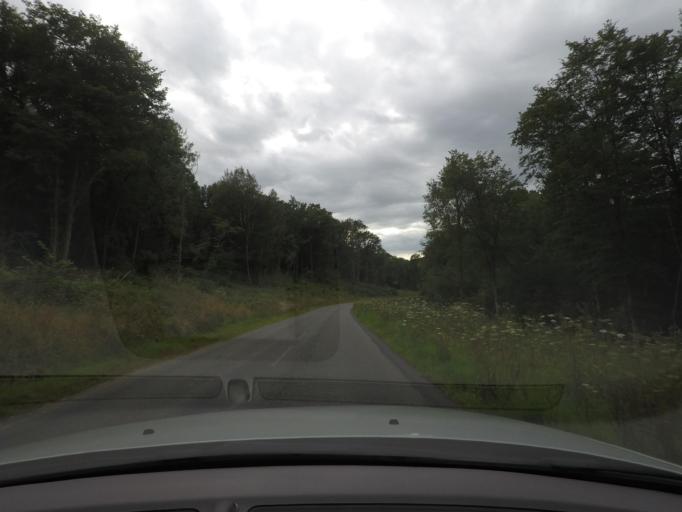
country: FR
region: Haute-Normandie
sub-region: Departement de l'Eure
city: Les Andelys
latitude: 49.2818
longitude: 1.3538
